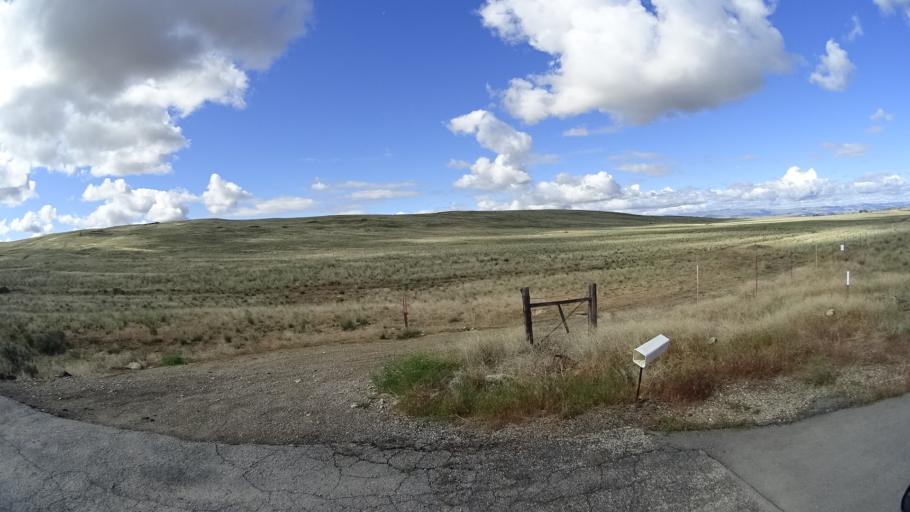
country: US
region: Idaho
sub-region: Ada County
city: Kuna
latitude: 43.4594
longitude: -116.4537
